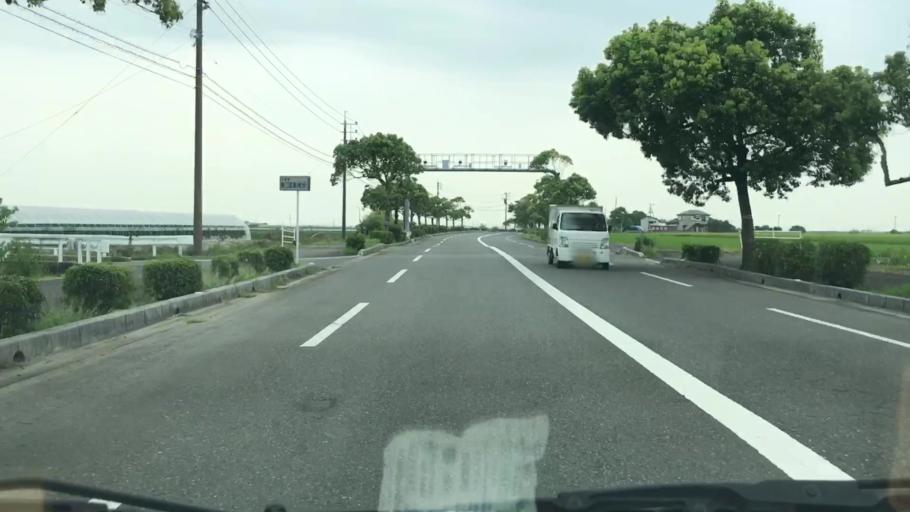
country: JP
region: Saga Prefecture
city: Okawa
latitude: 33.1939
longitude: 130.3036
